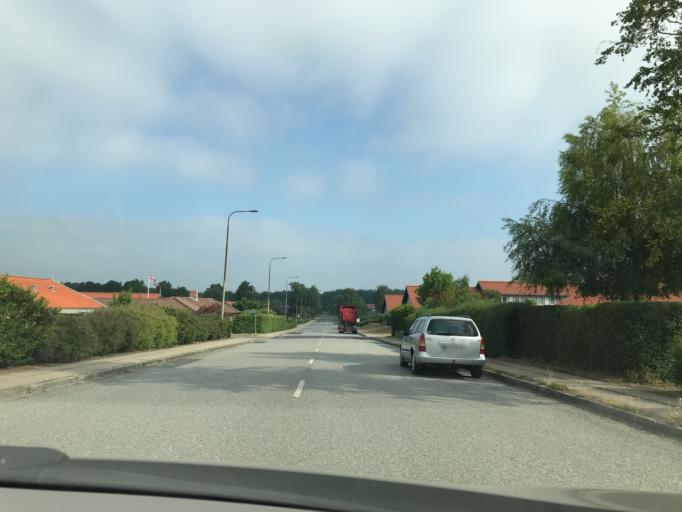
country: DK
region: South Denmark
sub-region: Odense Kommune
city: Bellinge
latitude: 55.3696
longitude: 10.3372
